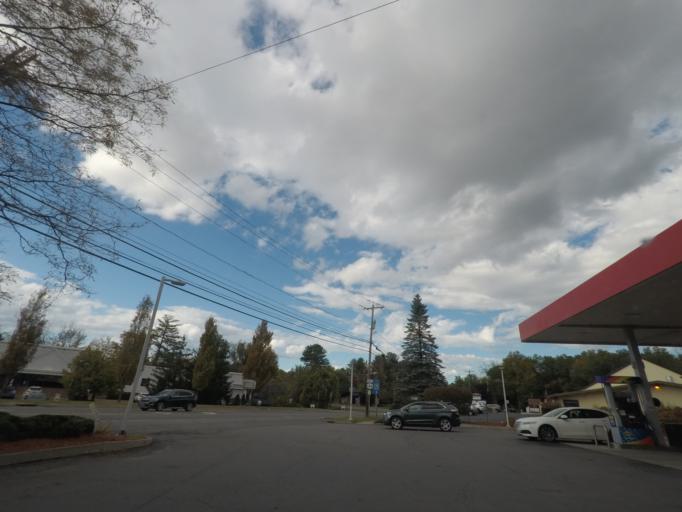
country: US
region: New York
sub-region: Albany County
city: Voorheesville
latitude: 42.7150
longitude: -73.9321
